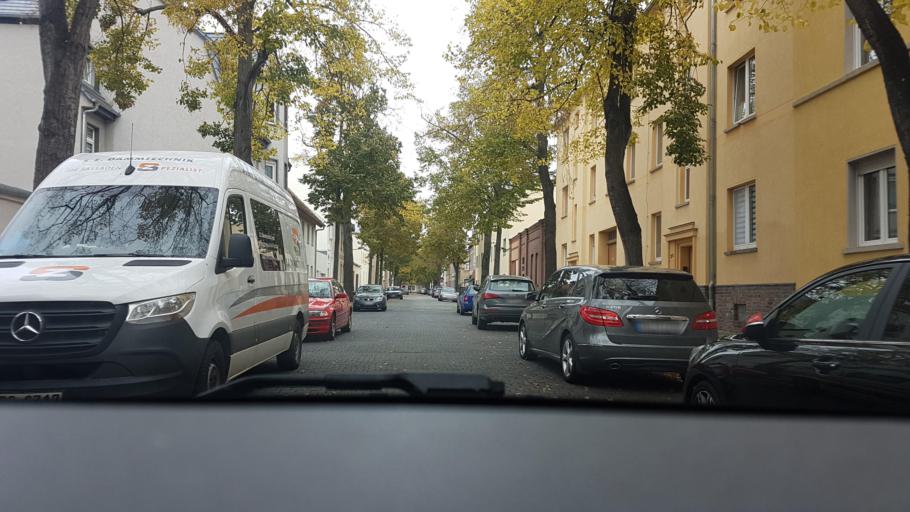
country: DE
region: Saxony-Anhalt
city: Bernburg
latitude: 51.7873
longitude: 11.7459
